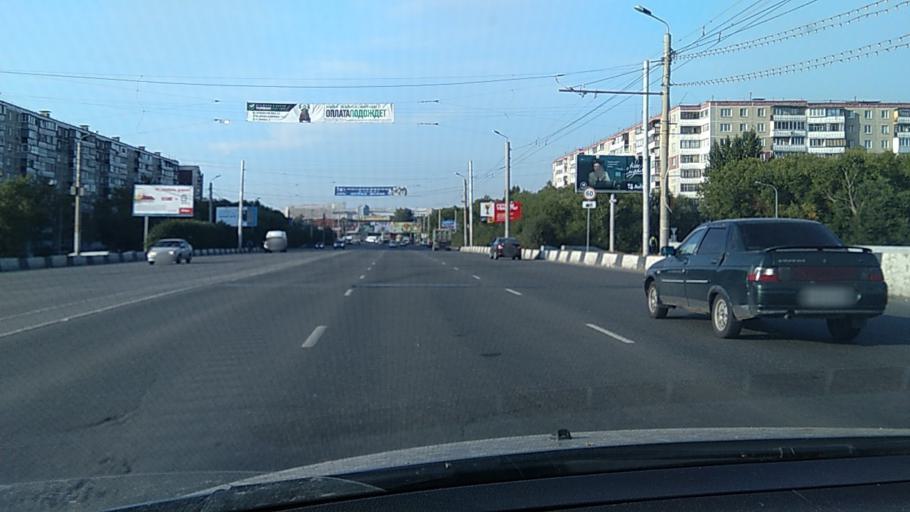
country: RU
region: Chelyabinsk
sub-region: Gorod Chelyabinsk
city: Chelyabinsk
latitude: 55.1749
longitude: 61.3583
